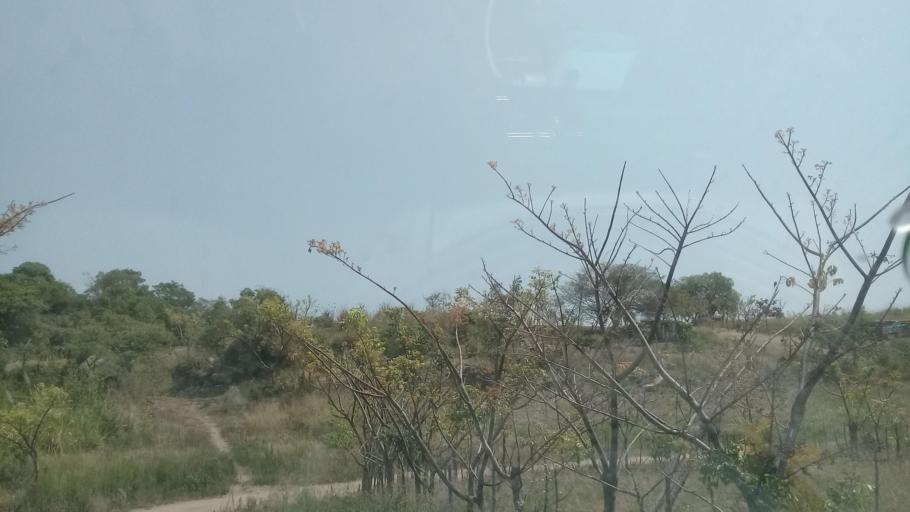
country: MX
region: Veracruz
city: El Castillo
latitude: 19.5652
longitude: -96.8440
